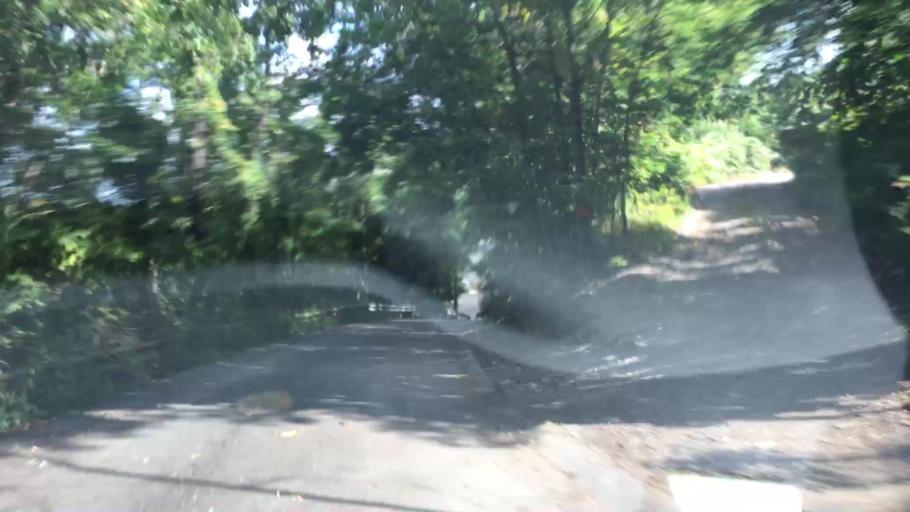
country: US
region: Pennsylvania
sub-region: Allegheny County
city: Millvale
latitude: 40.4990
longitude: -80.0026
